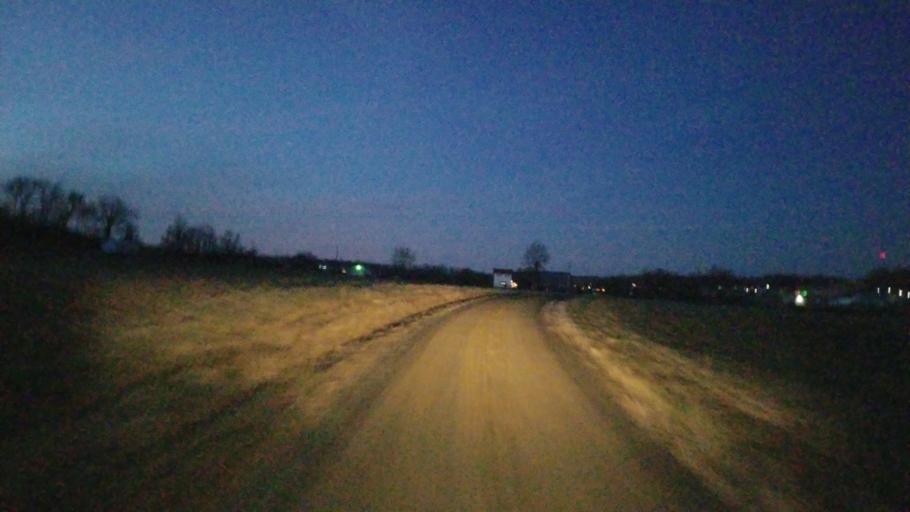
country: US
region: Pennsylvania
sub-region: Indiana County
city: Chevy Chase Heights
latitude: 40.8671
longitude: -79.2415
